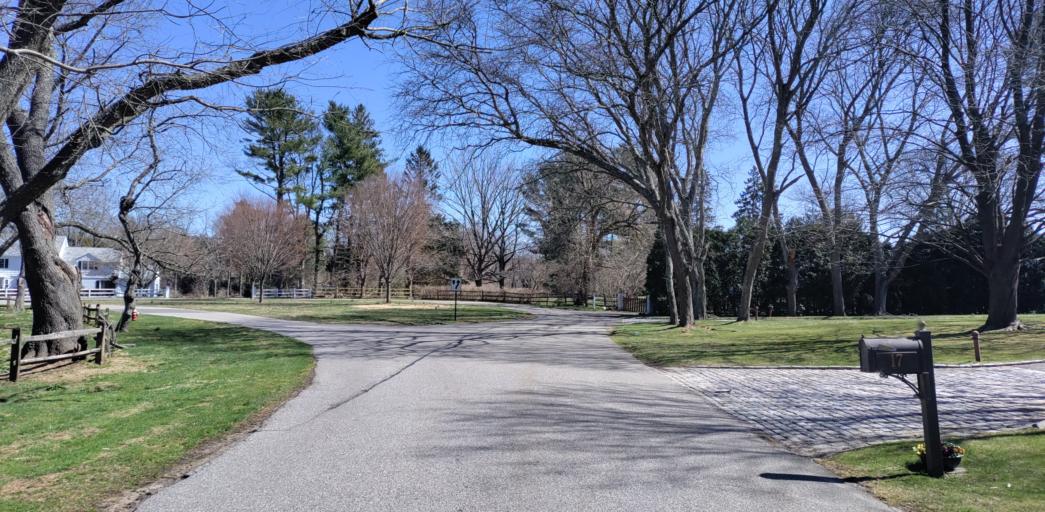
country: US
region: New York
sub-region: Nassau County
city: Old Brookville
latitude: 40.8269
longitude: -73.6024
